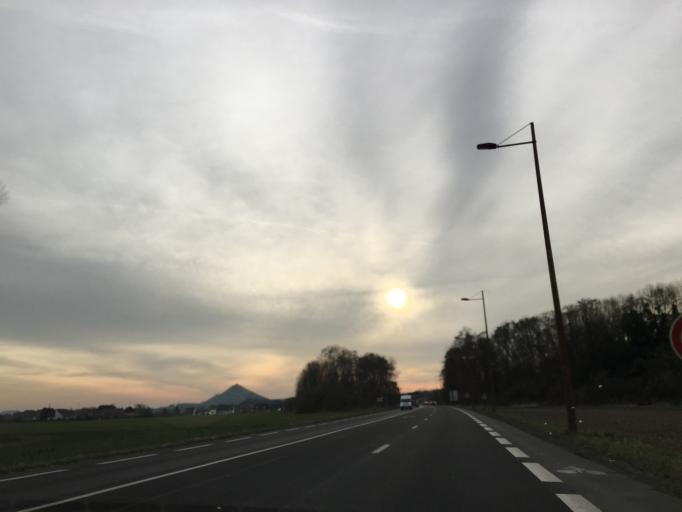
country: FR
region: Nord-Pas-de-Calais
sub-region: Departement du Pas-de-Calais
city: Montigny-en-Gohelle
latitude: 50.4379
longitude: 2.9478
